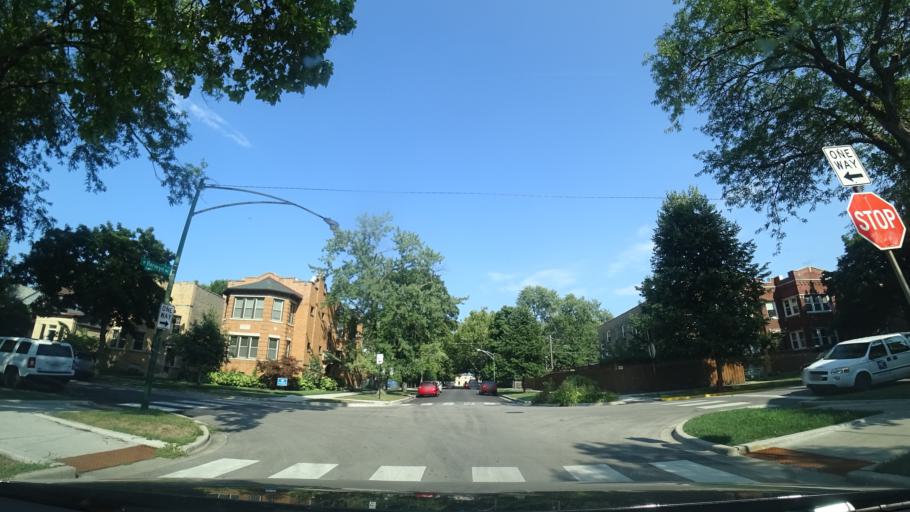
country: US
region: Illinois
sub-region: Cook County
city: Lincolnwood
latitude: 41.9776
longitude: -87.7114
